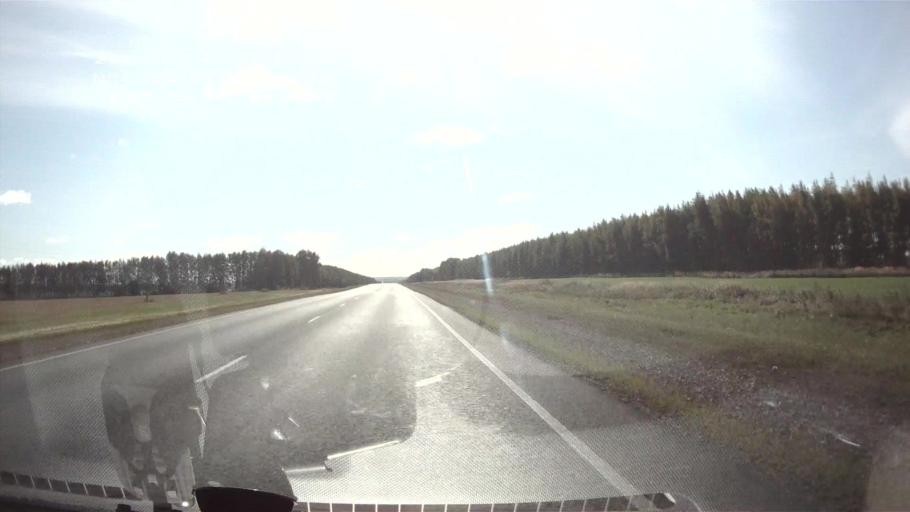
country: RU
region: Ulyanovsk
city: Tsil'na
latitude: 54.5533
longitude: 47.9380
